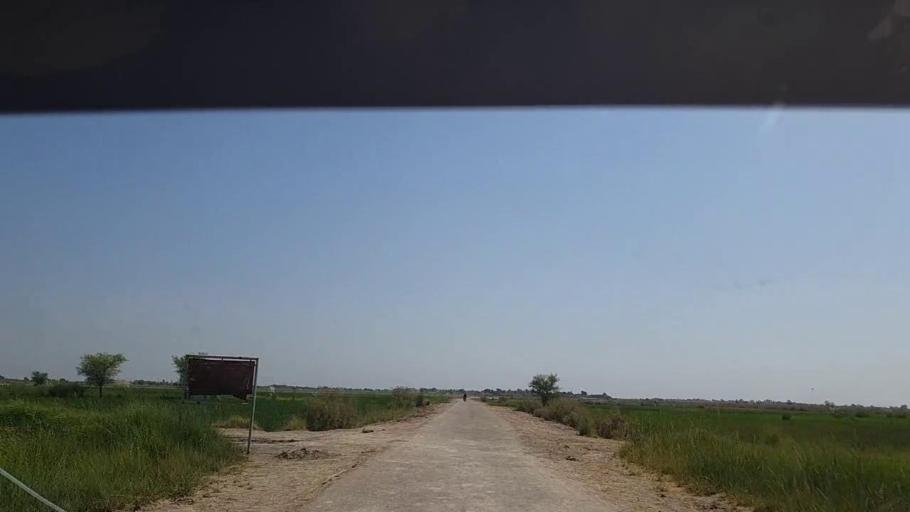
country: PK
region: Sindh
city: Kandhkot
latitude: 28.1799
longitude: 69.1591
